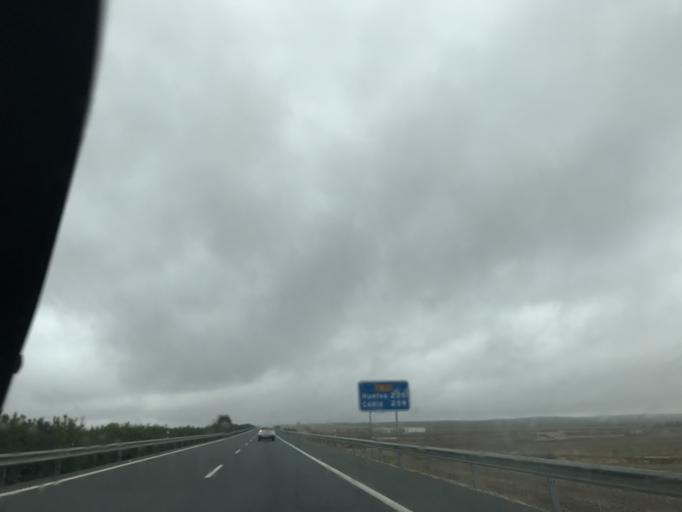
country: ES
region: Andalusia
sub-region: Provincia de Malaga
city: Fuente de Piedra
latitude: 37.1456
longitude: -4.7354
